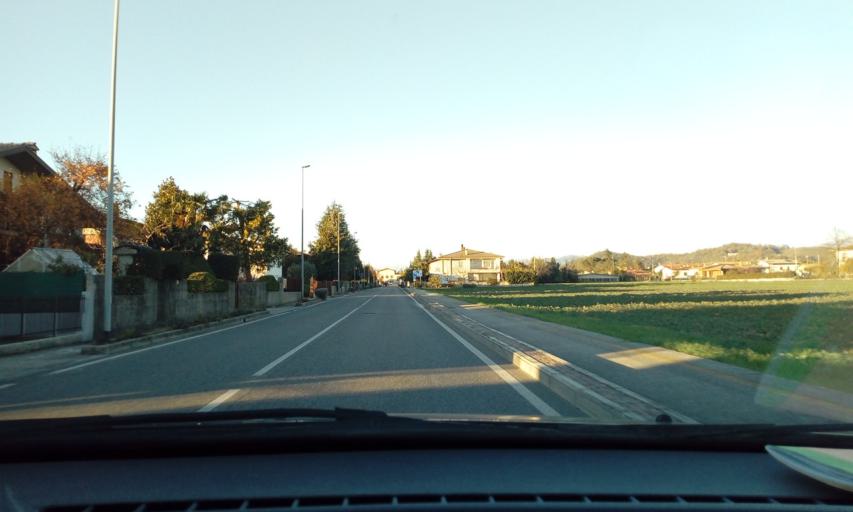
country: IT
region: Friuli Venezia Giulia
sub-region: Provincia di Udine
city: Corno di Rosazzo
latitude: 45.9849
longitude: 13.4466
